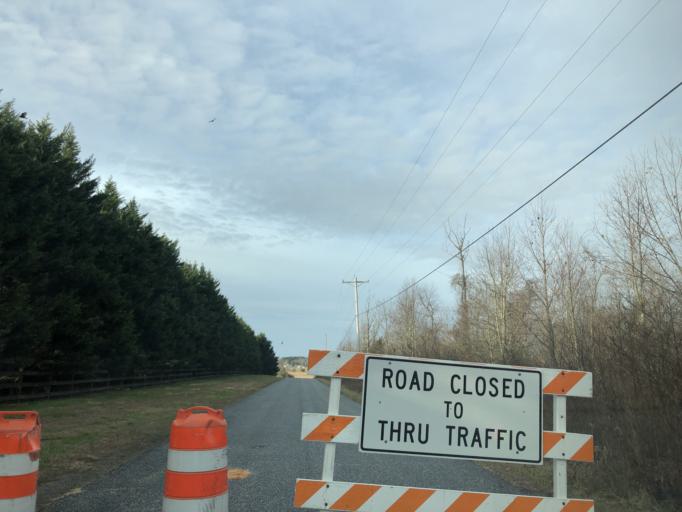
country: US
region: Delaware
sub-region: New Castle County
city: Middletown
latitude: 39.4529
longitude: -75.6423
